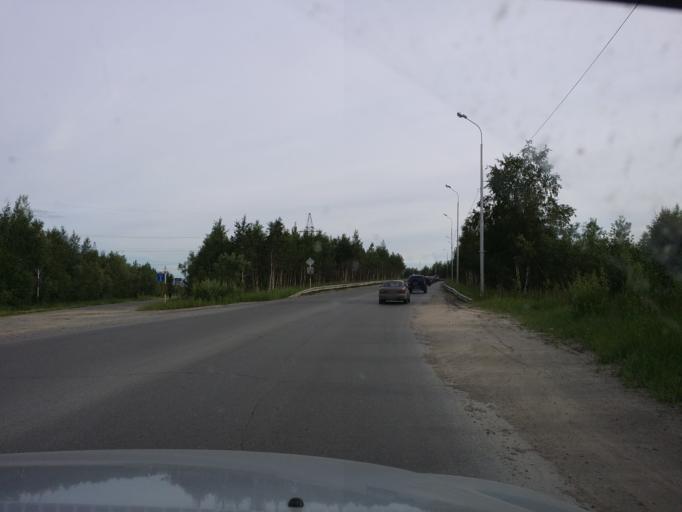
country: RU
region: Khanty-Mansiyskiy Avtonomnyy Okrug
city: Nizhnevartovsk
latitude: 60.9557
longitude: 76.6640
